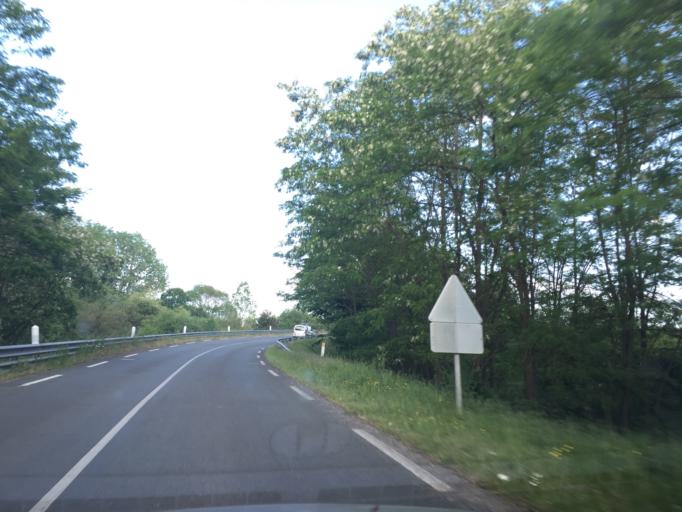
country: FR
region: Aquitaine
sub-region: Departement de la Gironde
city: Saint-Denis-de-Pile
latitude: 44.9733
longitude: -0.1959
